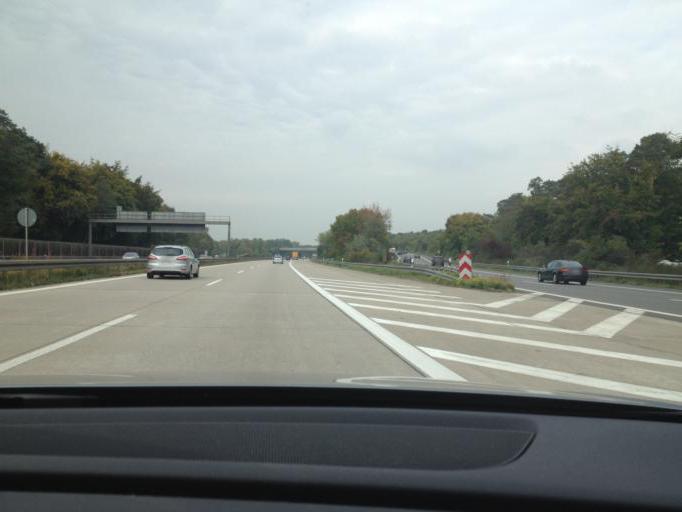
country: DE
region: Baden-Wuerttemberg
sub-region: Karlsruhe Region
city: Hockenheim
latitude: 49.3277
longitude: 8.5631
